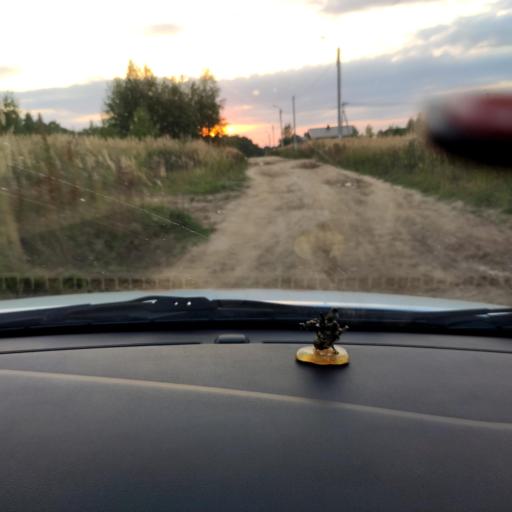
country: RU
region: Tatarstan
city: Vysokaya Gora
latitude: 55.8187
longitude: 49.3080
